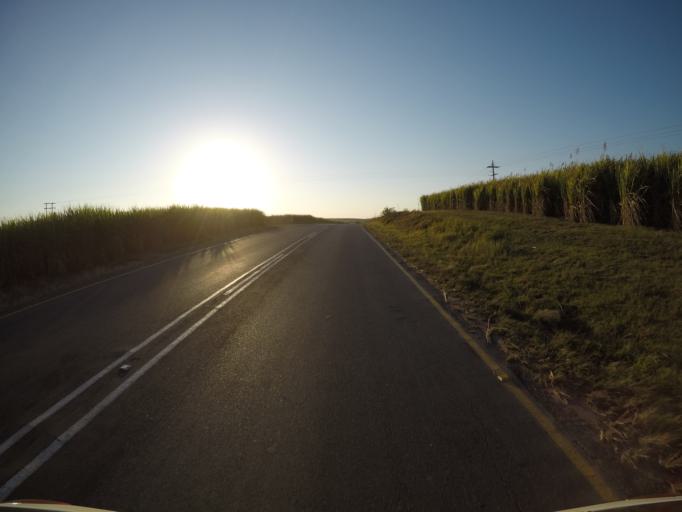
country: ZA
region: KwaZulu-Natal
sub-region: uThungulu District Municipality
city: eSikhawini
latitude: -28.9488
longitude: 31.7168
